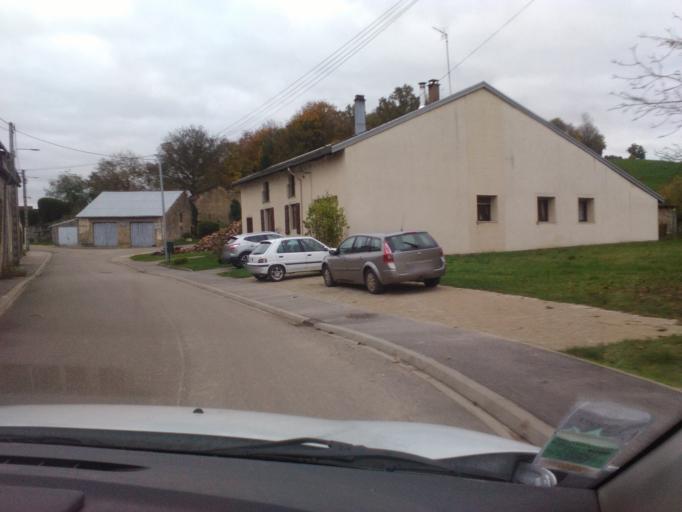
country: FR
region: Lorraine
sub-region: Departement des Vosges
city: Mirecourt
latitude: 48.3115
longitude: 6.2084
